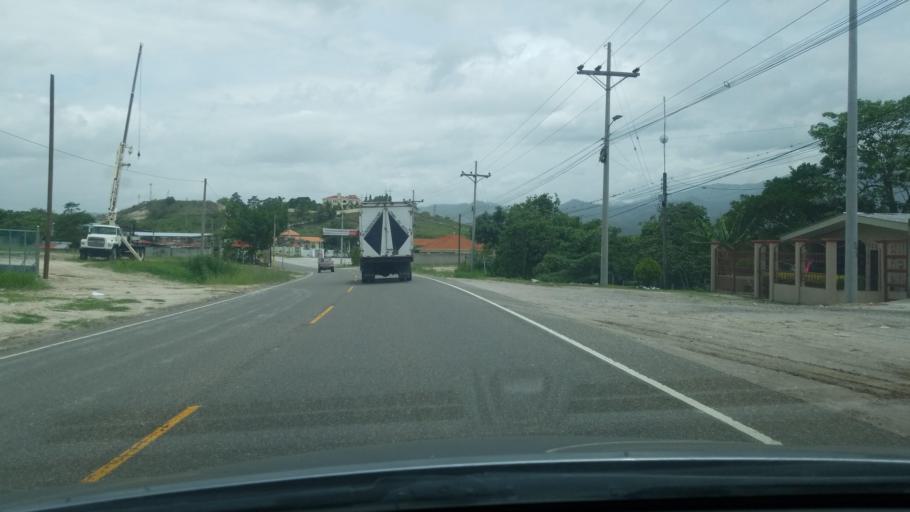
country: HN
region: Copan
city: Cucuyagua
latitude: 14.6650
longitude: -88.8696
